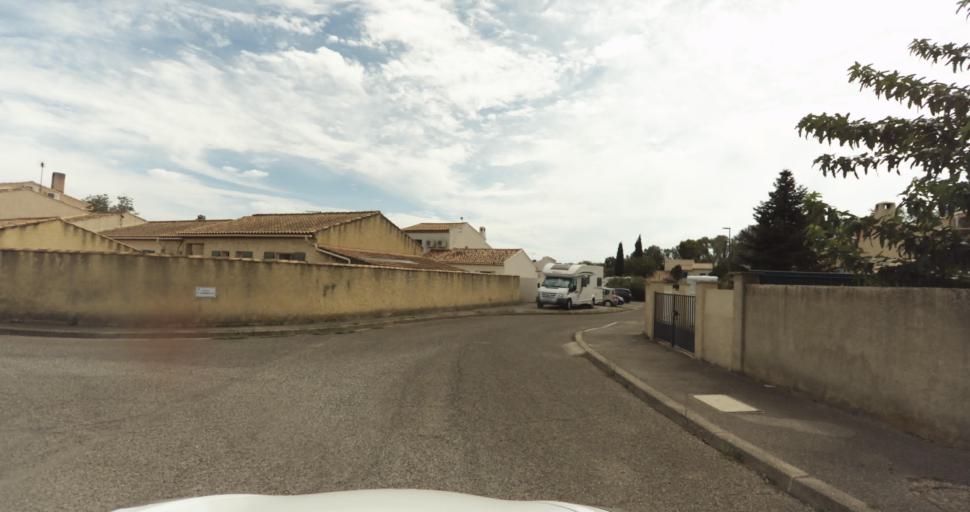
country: FR
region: Provence-Alpes-Cote d'Azur
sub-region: Departement des Bouches-du-Rhone
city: Miramas
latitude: 43.5775
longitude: 4.9924
